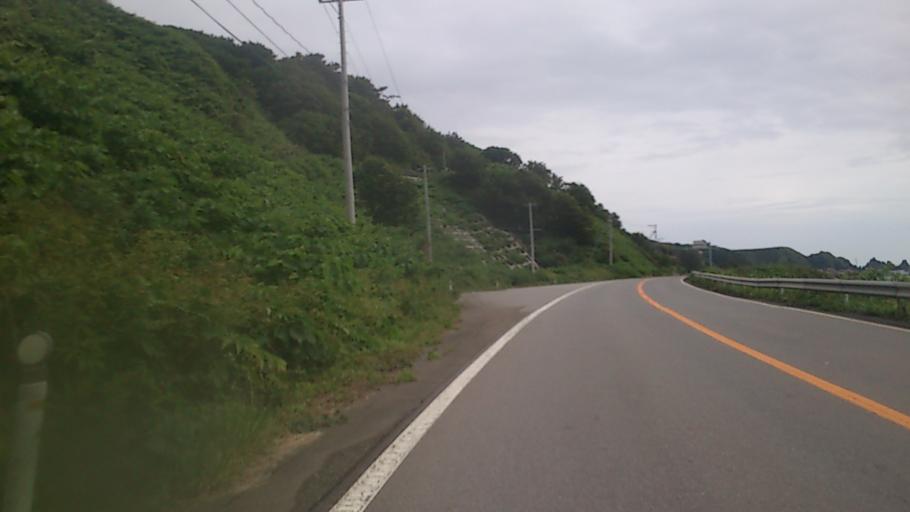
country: JP
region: Akita
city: Noshiromachi
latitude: 40.4440
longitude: 139.9403
